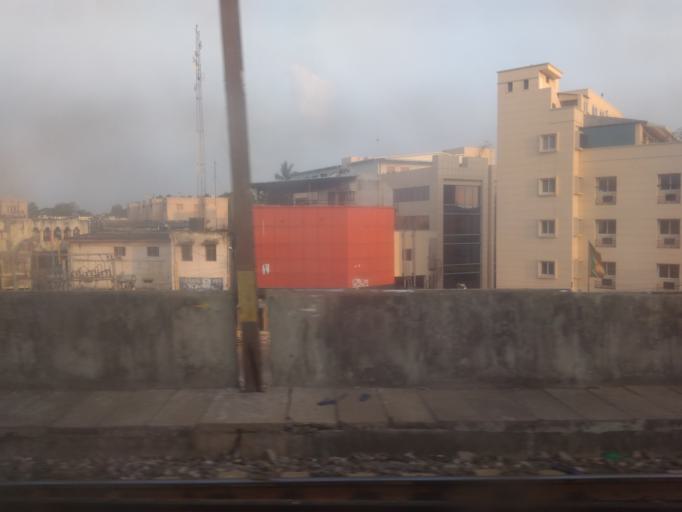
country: IN
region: Tamil Nadu
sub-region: Chennai
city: Gandhi Nagar
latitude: 13.0356
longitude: 80.2678
